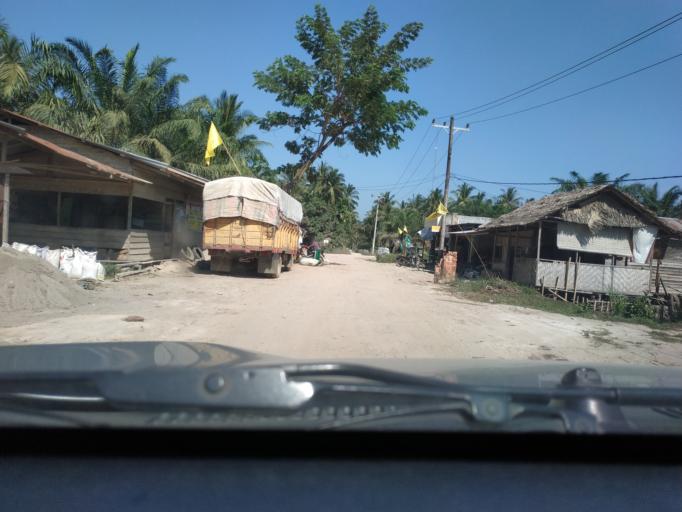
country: ID
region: North Sumatra
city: Tanjungbalai
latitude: 2.8497
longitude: 99.9436
